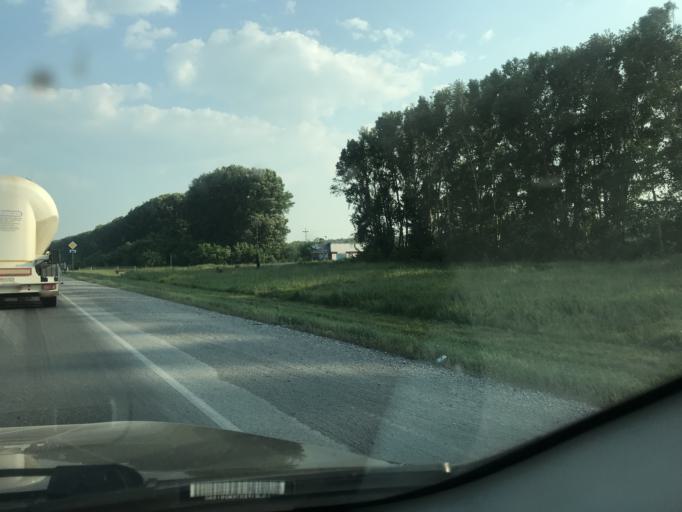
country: RU
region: Novosibirsk
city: Linevo
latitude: 54.5093
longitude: 83.3321
